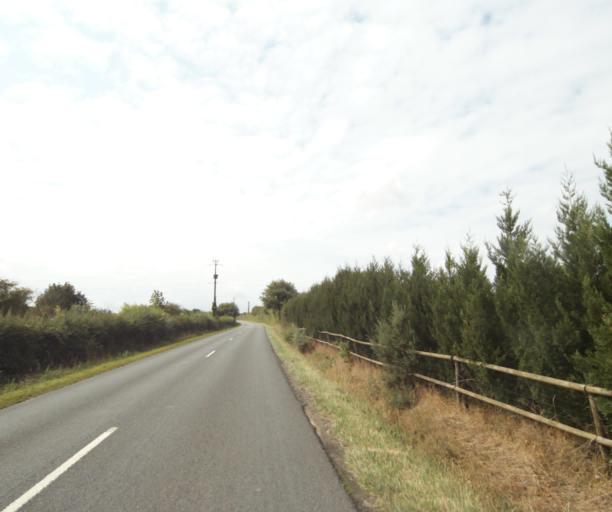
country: FR
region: Pays de la Loire
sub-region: Departement de la Sarthe
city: Sable-sur-Sarthe
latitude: 47.8204
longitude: -0.3185
